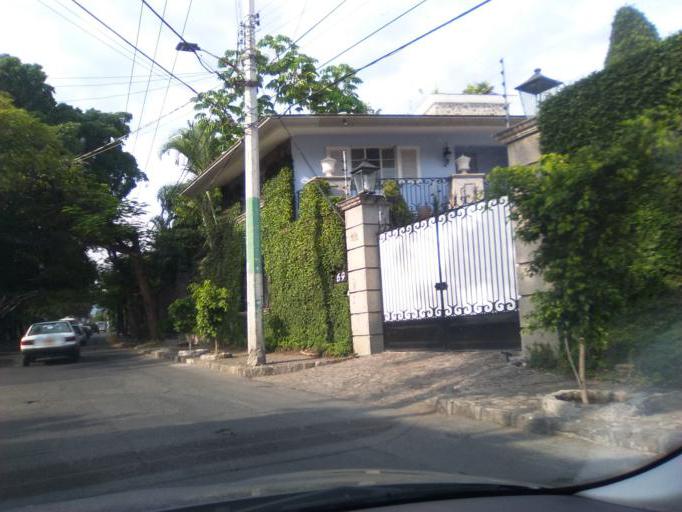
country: MX
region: Morelos
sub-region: Cuernavaca
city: Cuernavaca
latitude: 18.9035
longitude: -99.2267
